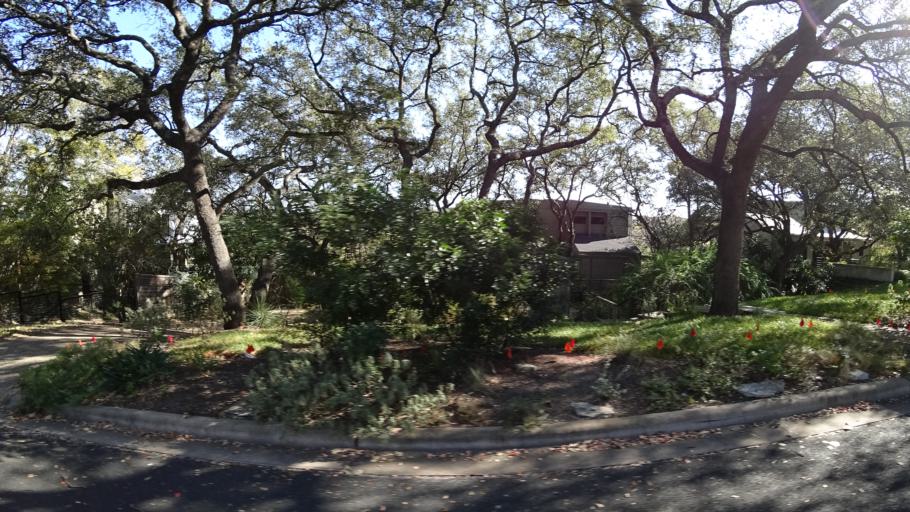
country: US
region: Texas
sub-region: Williamson County
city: Jollyville
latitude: 30.3820
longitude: -97.7598
